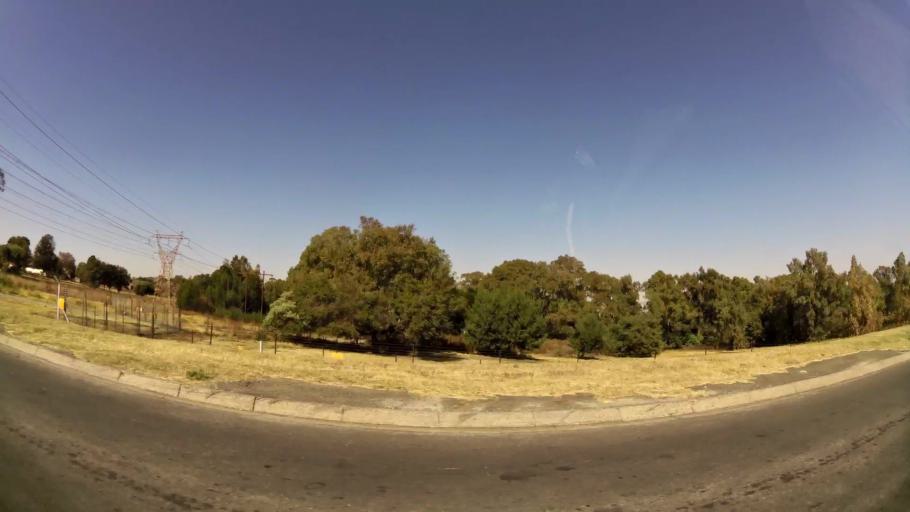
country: ZA
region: Gauteng
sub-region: City of Johannesburg Metropolitan Municipality
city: Modderfontein
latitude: -26.0865
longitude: 28.1816
